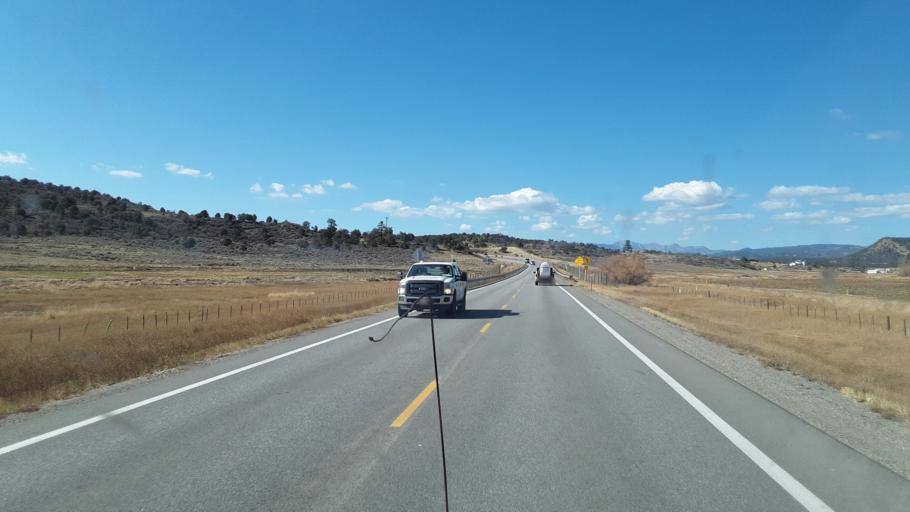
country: US
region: Colorado
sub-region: La Plata County
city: Bayfield
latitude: 37.2247
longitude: -107.6810
